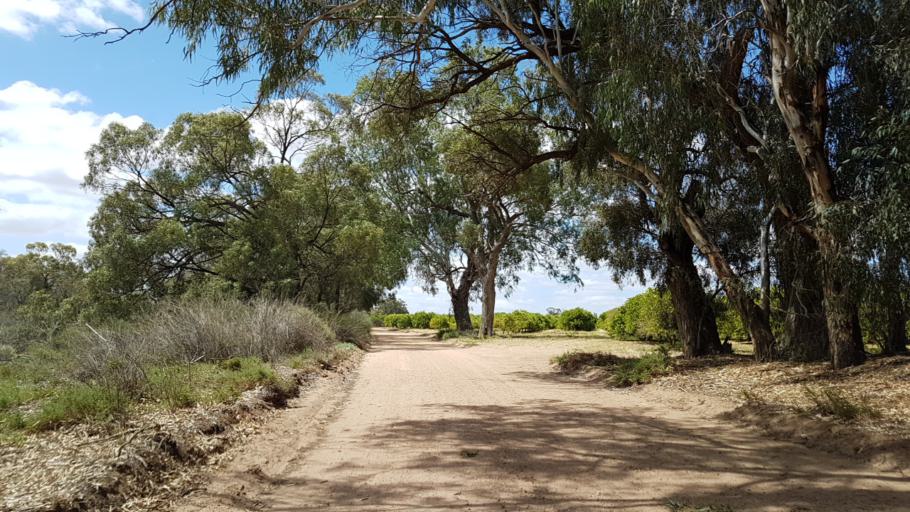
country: AU
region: South Australia
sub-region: Loxton Waikerie
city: Waikerie
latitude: -34.1764
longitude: 140.0212
